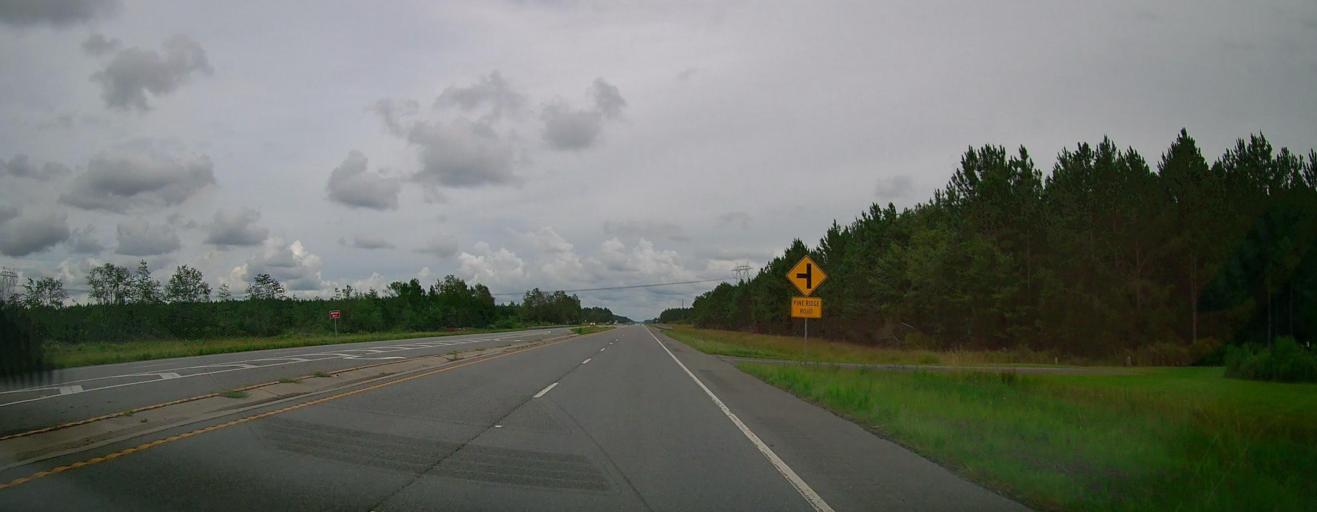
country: US
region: Georgia
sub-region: Appling County
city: Baxley
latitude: 31.7572
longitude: -82.2871
